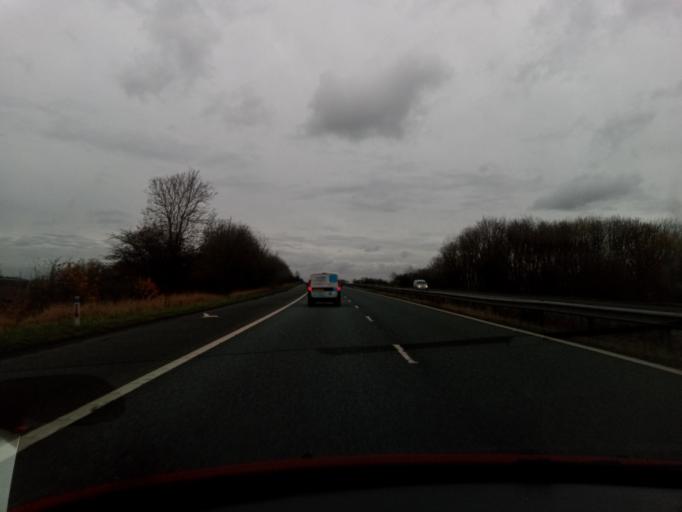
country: GB
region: England
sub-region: Darlington
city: High Coniscliffe
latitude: 54.5444
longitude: -1.6050
